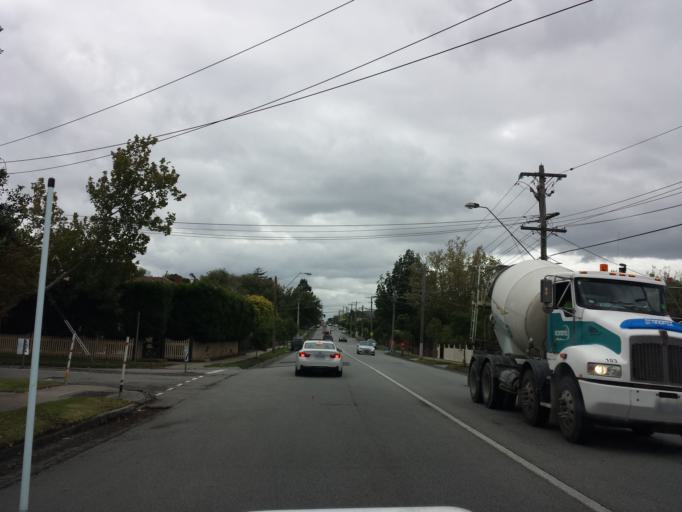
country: AU
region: Victoria
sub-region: Stonnington
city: Malvern East
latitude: -37.8702
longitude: 145.0492
